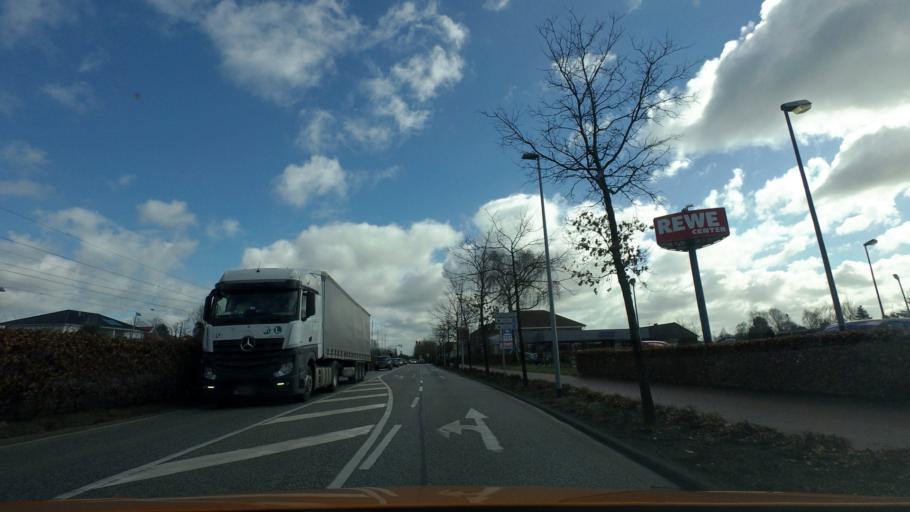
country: DE
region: Lower Saxony
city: Bad Zwischenahn
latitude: 53.1818
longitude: 8.0066
